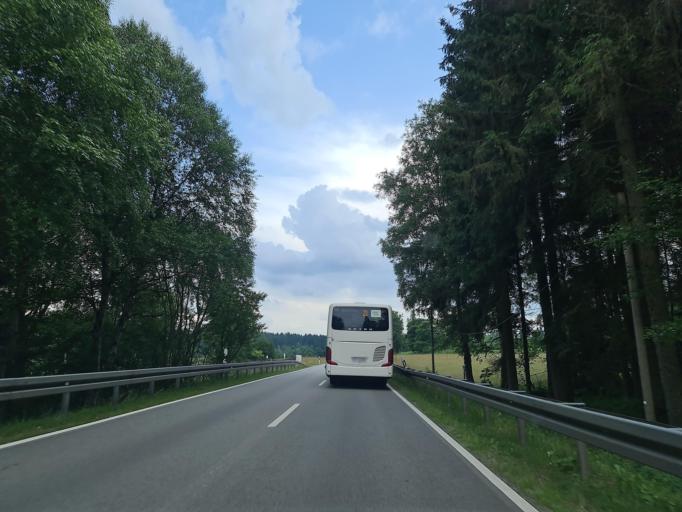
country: DE
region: Saxony
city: Hammerbrucke
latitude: 50.4211
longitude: 12.3988
